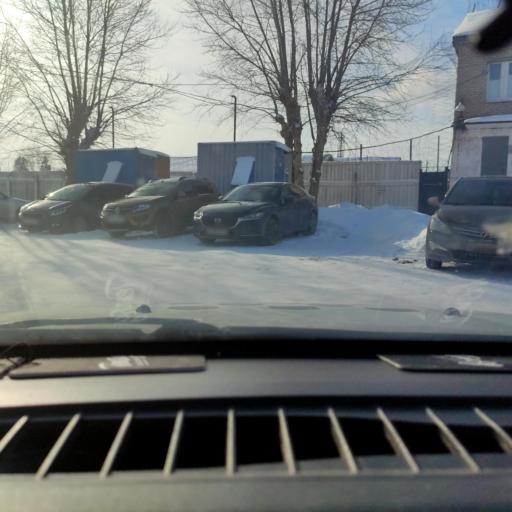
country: RU
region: Perm
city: Gamovo
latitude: 57.8759
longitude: 56.0846
